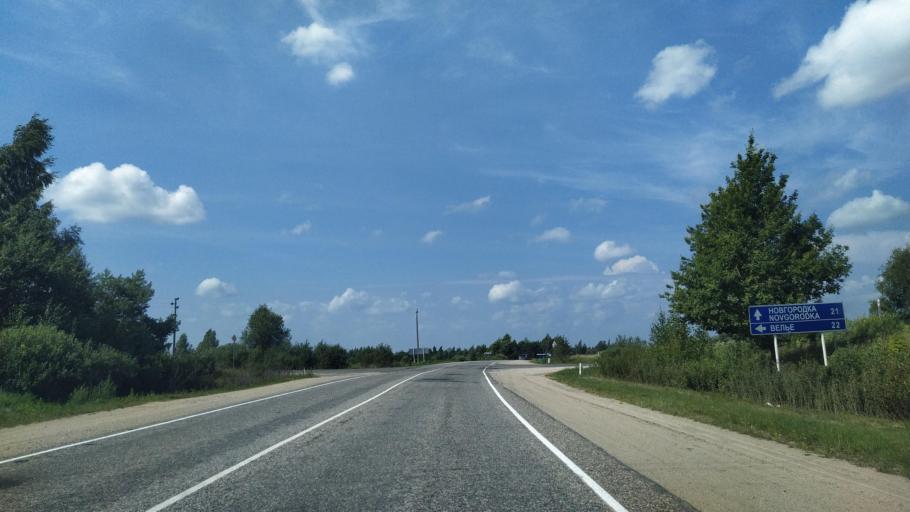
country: RU
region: Pskov
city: Pushkinskiye Gory
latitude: 57.0110
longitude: 28.9054
